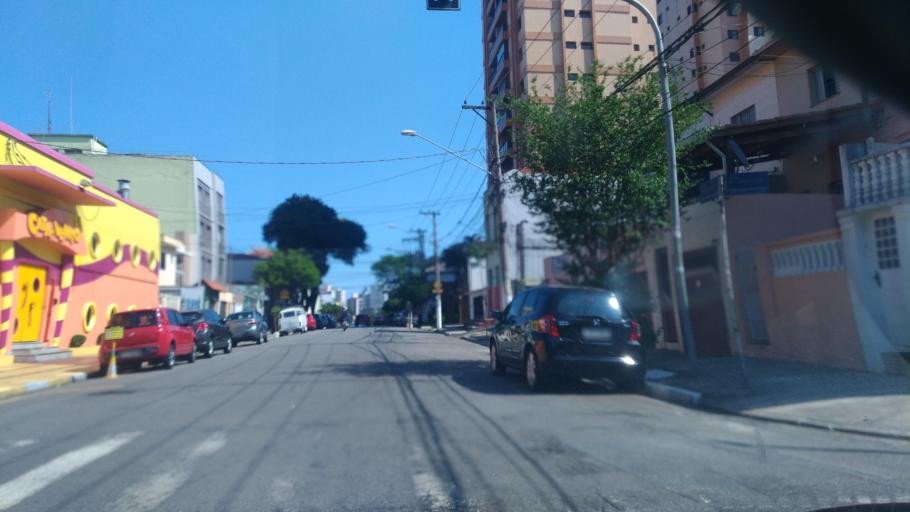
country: BR
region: Sao Paulo
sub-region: Sao Caetano Do Sul
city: Sao Caetano do Sul
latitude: -23.5971
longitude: -46.6032
